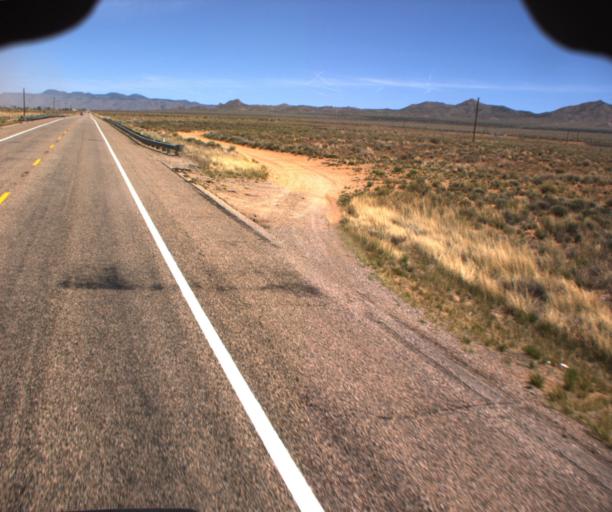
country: US
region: Arizona
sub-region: Mohave County
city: New Kingman-Butler
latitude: 35.3611
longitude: -113.8730
